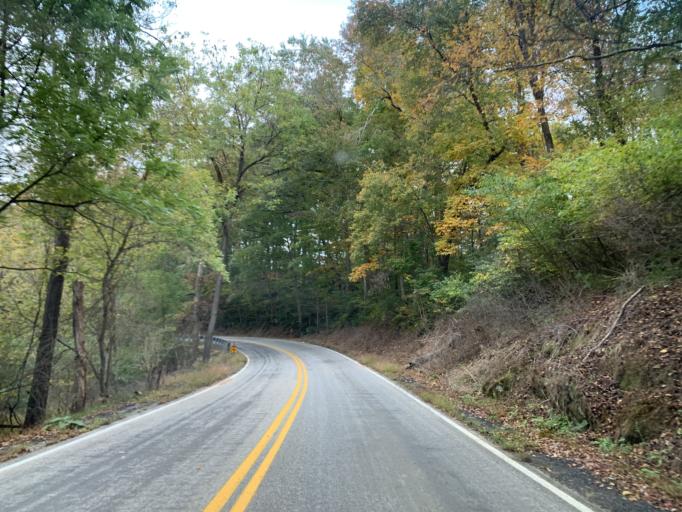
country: US
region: Pennsylvania
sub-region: York County
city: Susquehanna Trails
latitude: 39.7737
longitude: -76.4240
